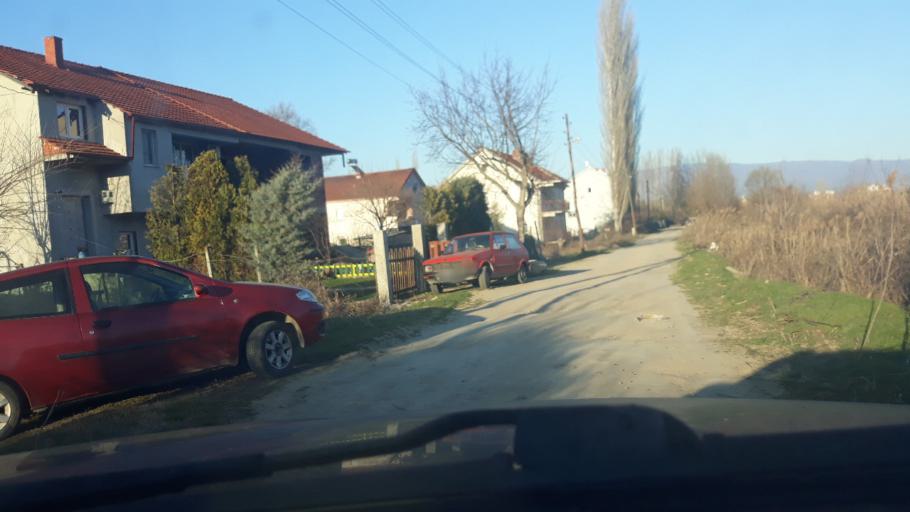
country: MK
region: Strumica
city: Strumica
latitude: 41.4457
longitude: 22.6289
